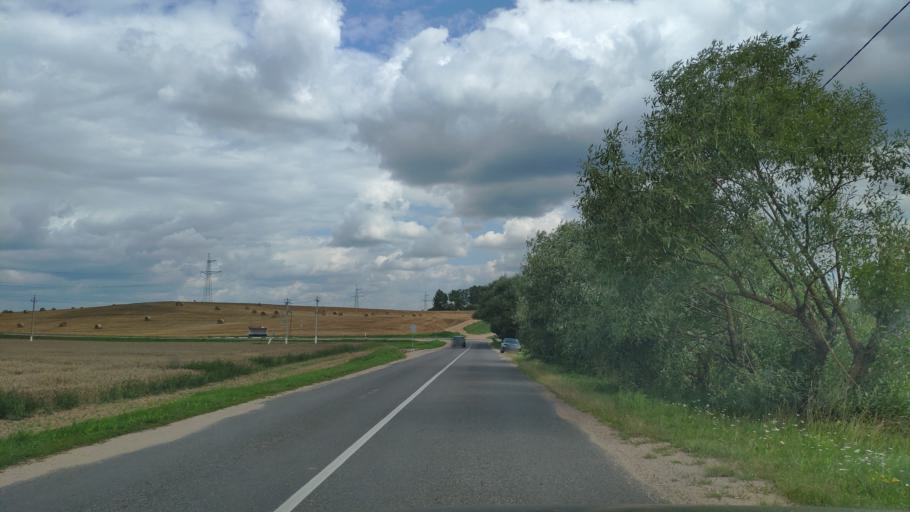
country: BY
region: Minsk
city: Khatsyezhyna
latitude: 53.8696
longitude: 27.3162
